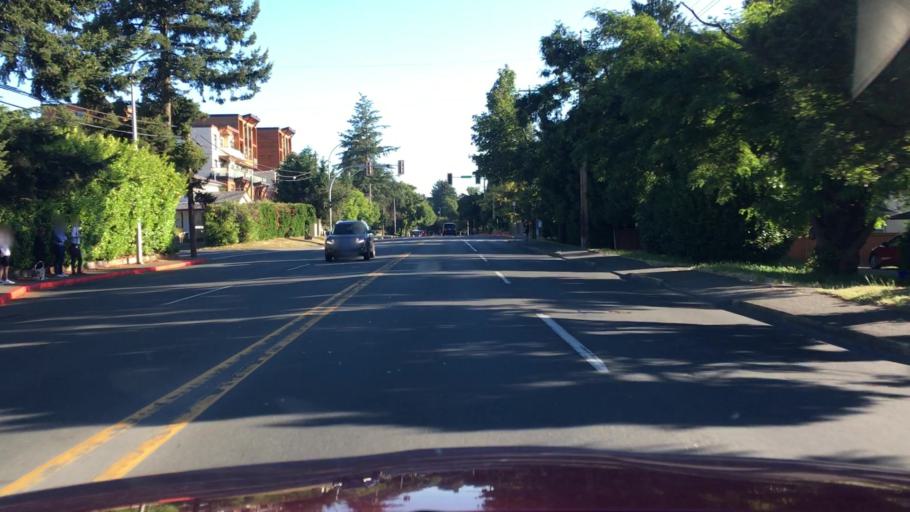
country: CA
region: British Columbia
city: Oak Bay
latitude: 48.4722
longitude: -123.3326
